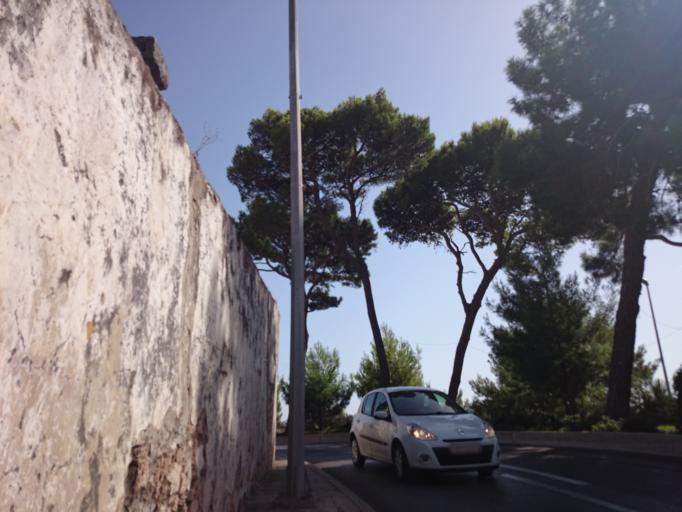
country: HR
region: Dubrovacko-Neretvanska
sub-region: Grad Dubrovnik
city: Dubrovnik
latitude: 42.6465
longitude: 18.0953
